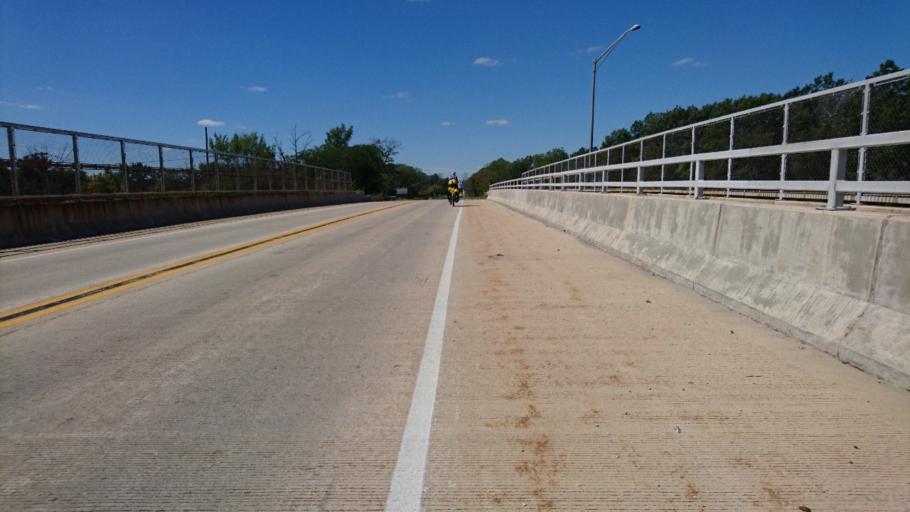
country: US
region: Illinois
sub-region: Cook County
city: Glenwood
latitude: 41.5427
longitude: -87.5822
